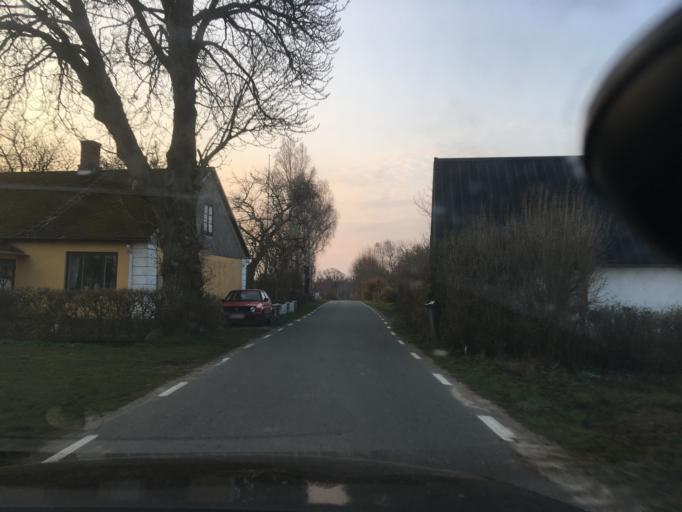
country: SE
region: Skane
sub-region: Ystads Kommun
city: Kopingebro
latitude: 55.4023
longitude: 14.1623
